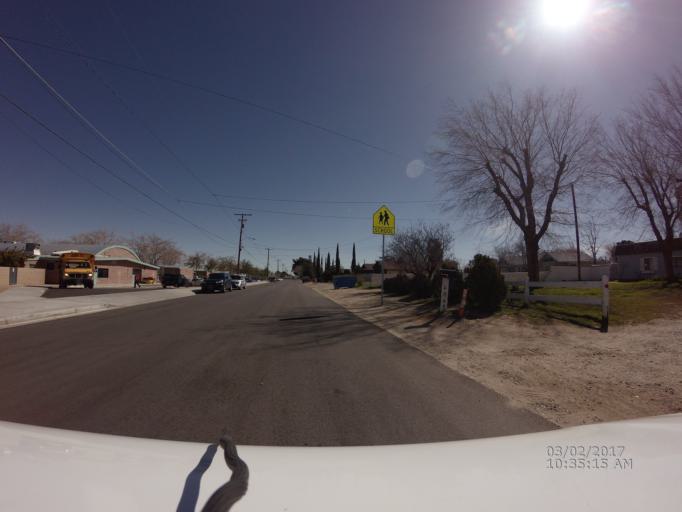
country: US
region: California
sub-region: Los Angeles County
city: Quartz Hill
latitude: 34.6419
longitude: -118.2180
